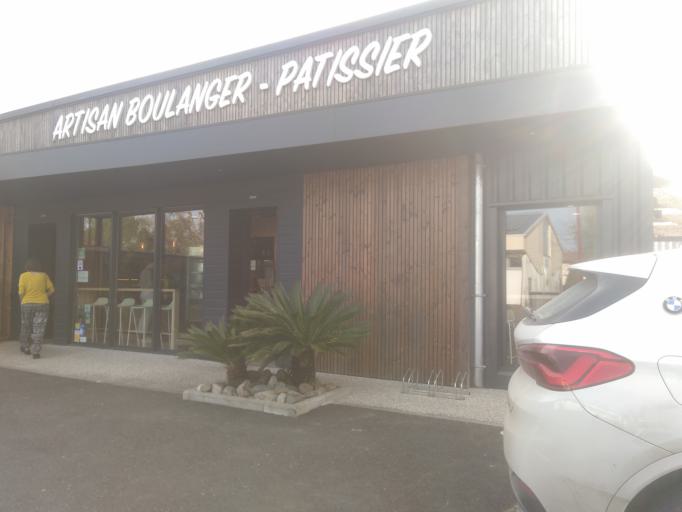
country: FR
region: Aquitaine
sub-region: Departement des Pyrenees-Atlantiques
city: Boucau
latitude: 43.5164
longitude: -1.4296
